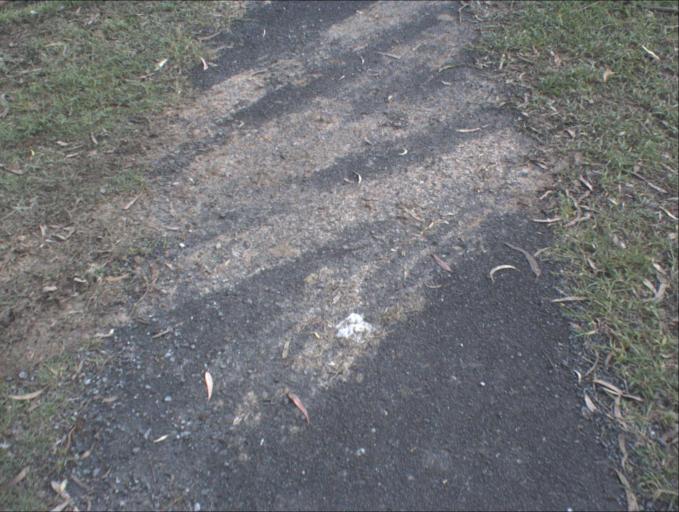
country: AU
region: Queensland
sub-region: Logan
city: Cedar Vale
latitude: -27.8332
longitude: 153.0283
